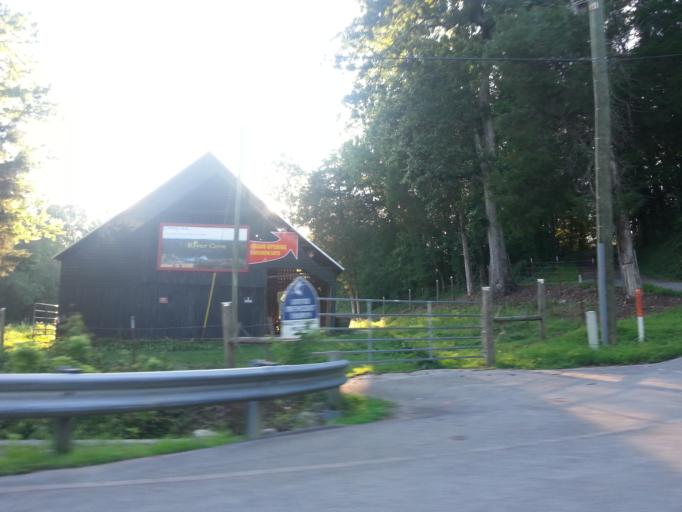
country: US
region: Tennessee
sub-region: Loudon County
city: Greenback
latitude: 35.7081
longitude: -84.2303
